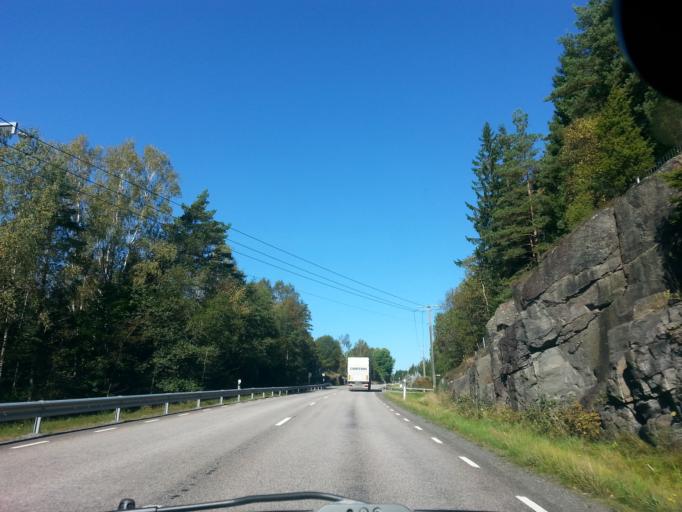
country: SE
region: Vaestra Goetaland
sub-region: Harryda Kommun
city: Hindas
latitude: 57.6330
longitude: 12.4106
